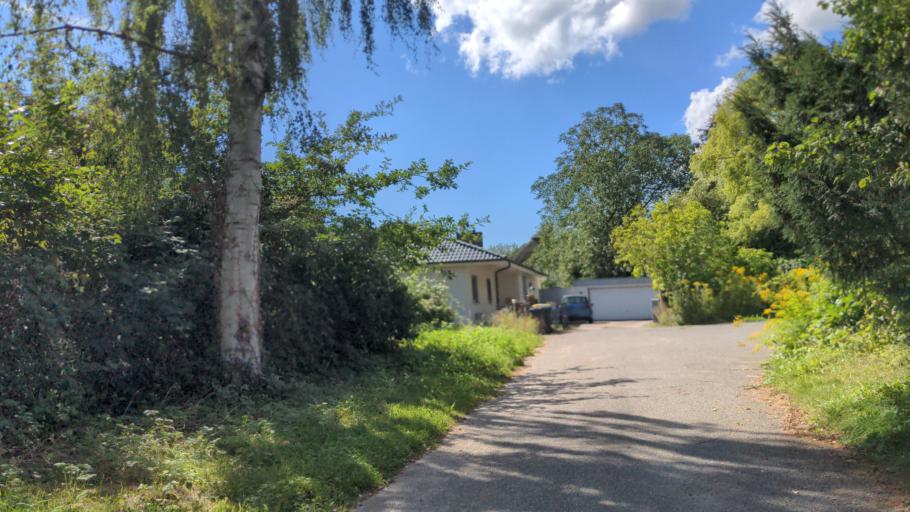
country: DE
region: Schleswig-Holstein
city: Lensahn
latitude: 54.2158
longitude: 10.8724
